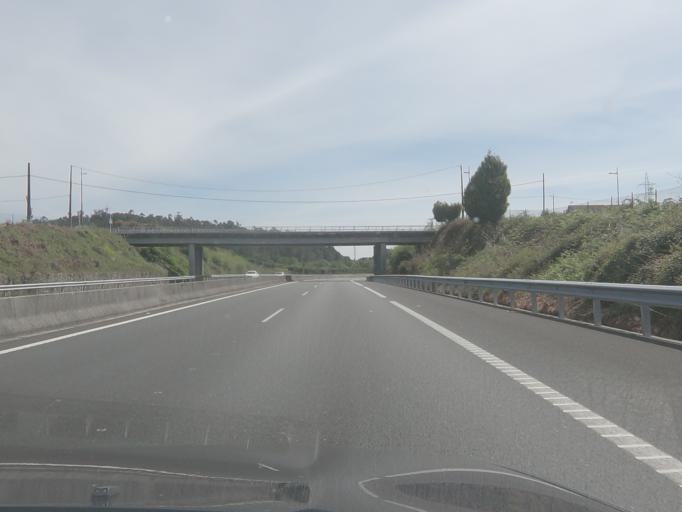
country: ES
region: Galicia
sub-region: Provincia de Pontevedra
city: Valga
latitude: 42.6680
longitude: -8.6337
